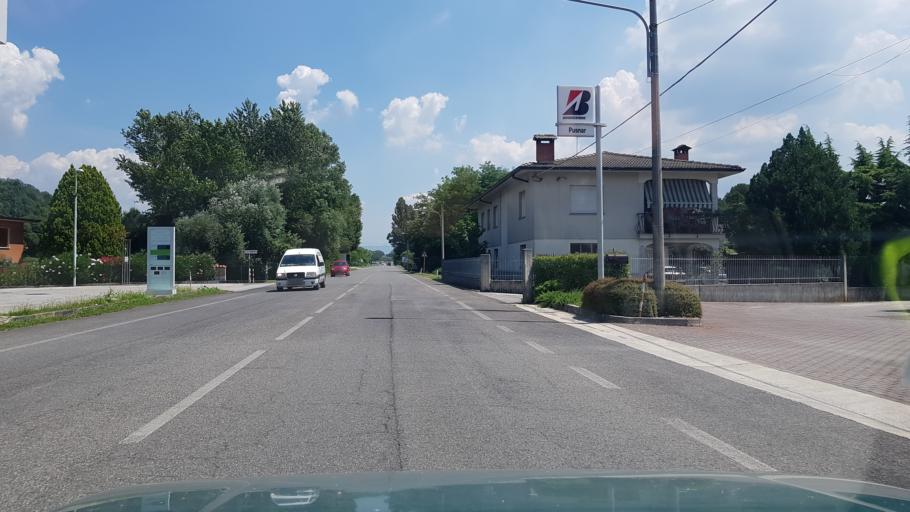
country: IT
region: Friuli Venezia Giulia
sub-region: Provincia di Gorizia
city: Farra d'Isonzo
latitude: 45.9043
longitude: 13.5368
